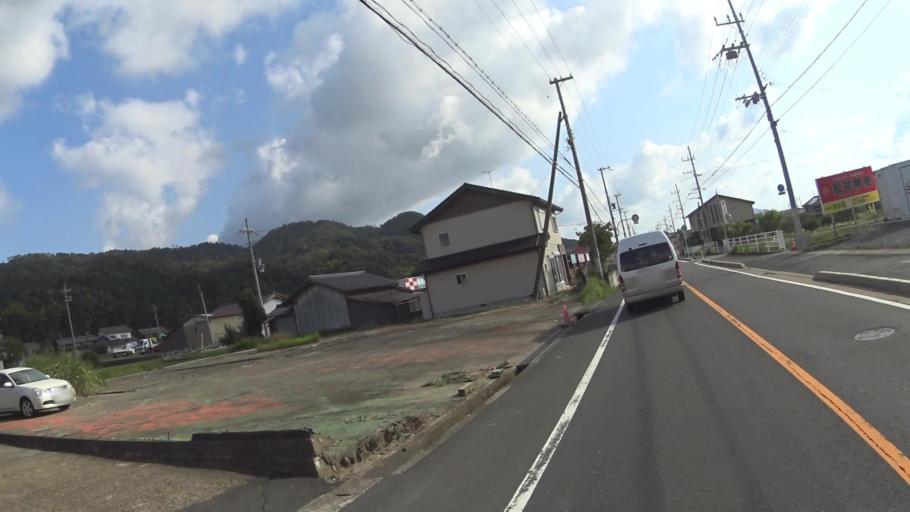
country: JP
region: Kyoto
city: Miyazu
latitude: 35.5775
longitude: 135.1822
